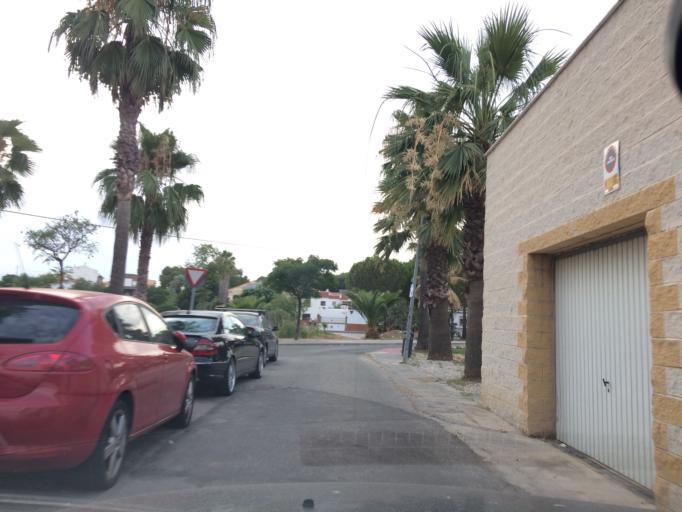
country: ES
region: Andalusia
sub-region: Provincia de Malaga
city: Estacion de Cartama
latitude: 36.7295
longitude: -4.5715
